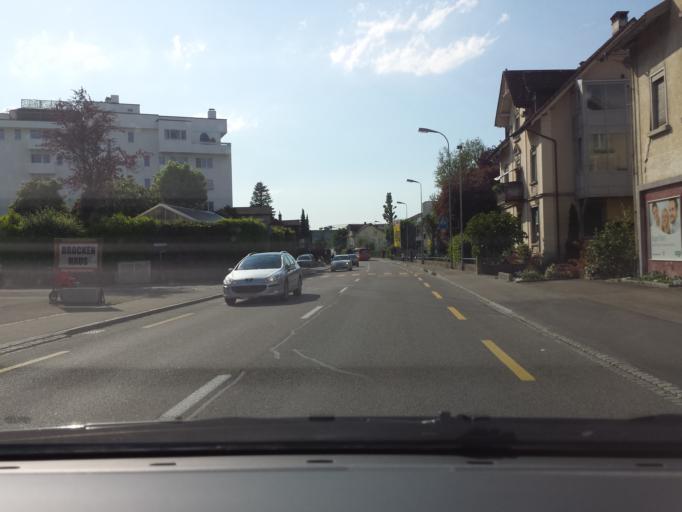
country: CH
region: Thurgau
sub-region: Arbon District
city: Arbon
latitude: 47.5183
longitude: 9.4272
